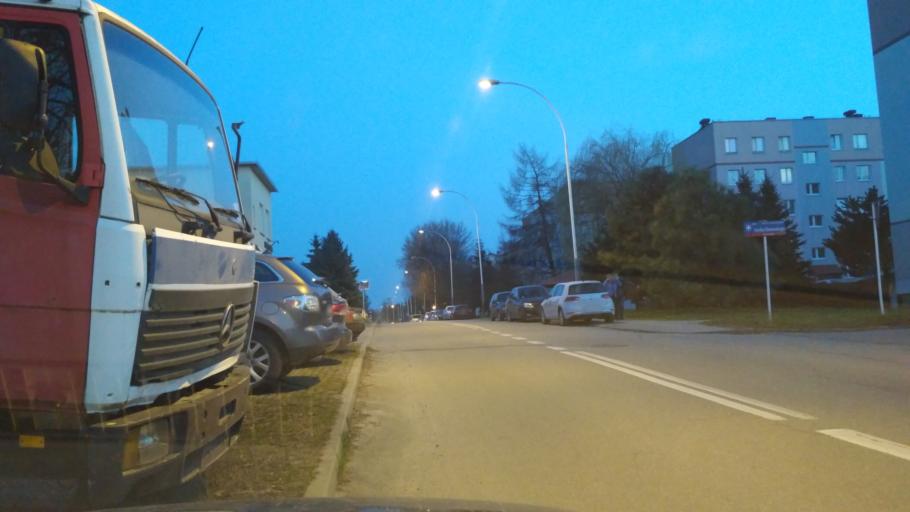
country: PL
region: Subcarpathian Voivodeship
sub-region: Rzeszow
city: Rzeszow
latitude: 50.0623
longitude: 21.9843
